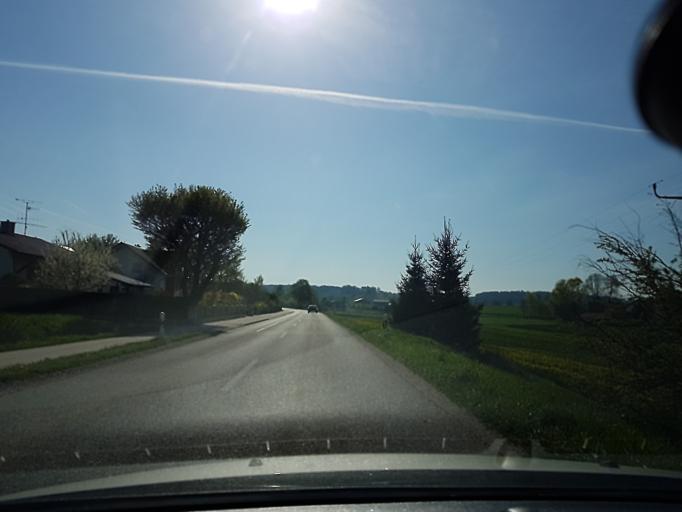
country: DE
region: Bavaria
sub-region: Lower Bavaria
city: Furth
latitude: 48.4048
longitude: 12.3836
